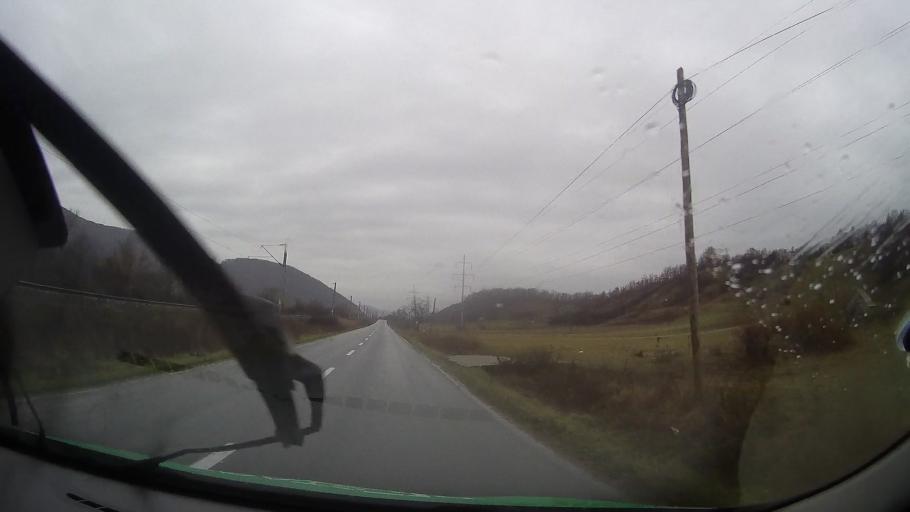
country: RO
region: Bistrita-Nasaud
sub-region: Municipiul Bistrita
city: Viisoara
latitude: 47.0490
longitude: 24.4581
